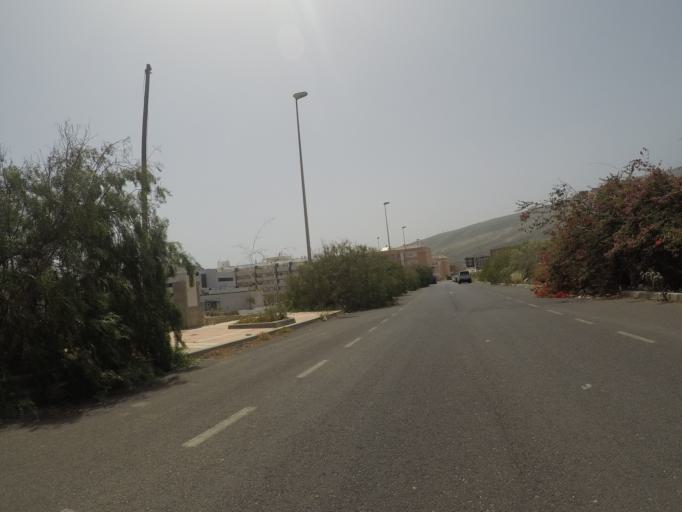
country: ES
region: Canary Islands
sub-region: Provincia de Santa Cruz de Tenerife
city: Candelaria
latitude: 28.2979
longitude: -16.3748
